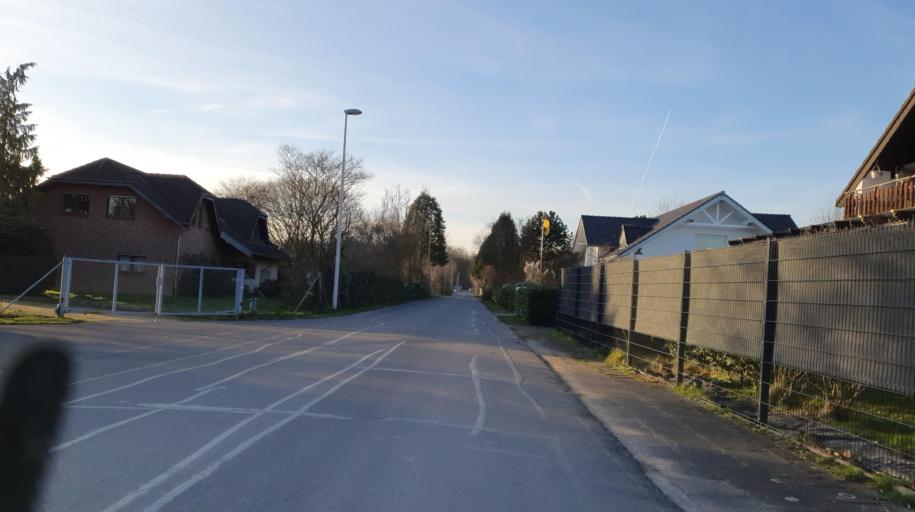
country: DE
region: North Rhine-Westphalia
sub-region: Regierungsbezirk Dusseldorf
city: Dormagen
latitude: 51.0718
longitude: 6.7736
